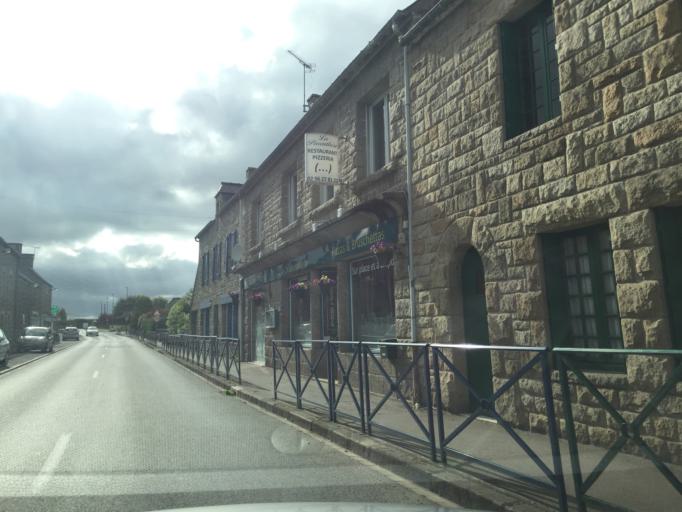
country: FR
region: Brittany
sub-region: Departement des Cotes-d'Armor
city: Crehen
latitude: 48.5798
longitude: -2.2218
